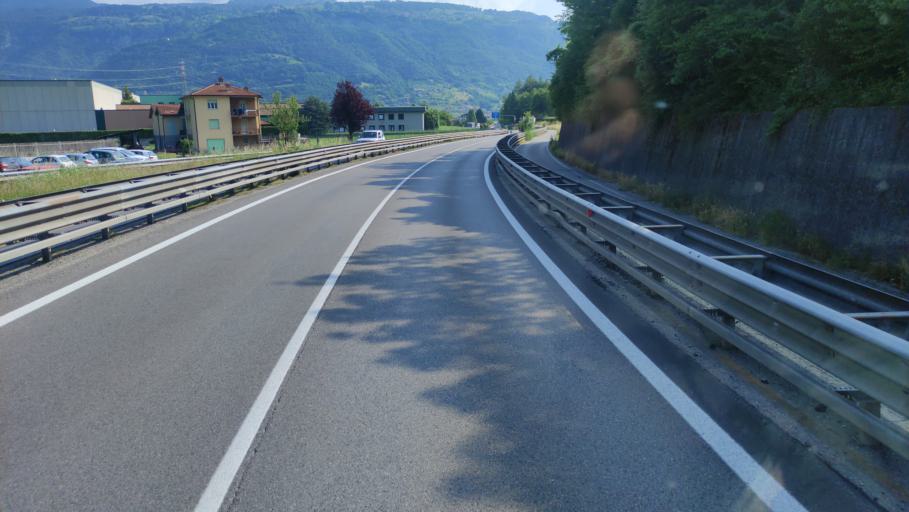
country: IT
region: Lombardy
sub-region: Provincia di Bergamo
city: Sovere
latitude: 45.8056
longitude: 10.0225
